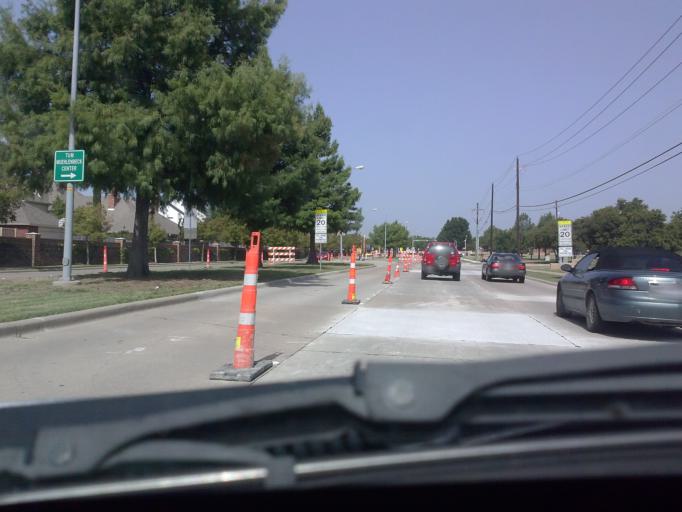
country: US
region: Texas
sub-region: Denton County
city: The Colony
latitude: 33.0452
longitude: -96.8195
